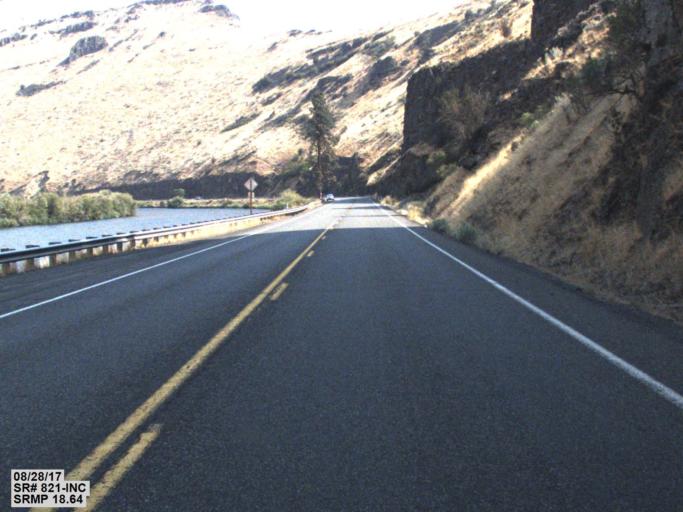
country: US
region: Washington
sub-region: Kittitas County
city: Kittitas
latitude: 46.8773
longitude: -120.4909
